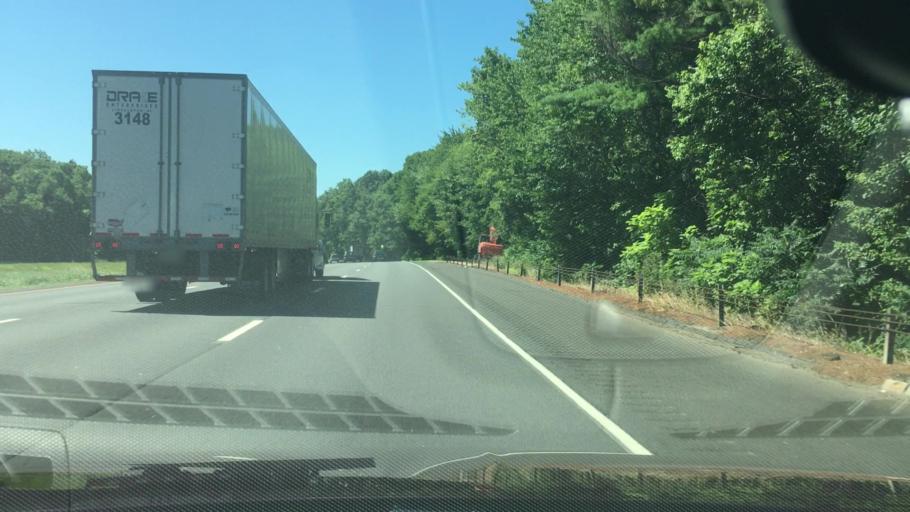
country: US
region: Connecticut
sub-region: New Haven County
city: Wolcott
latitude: 41.5971
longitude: -72.9036
